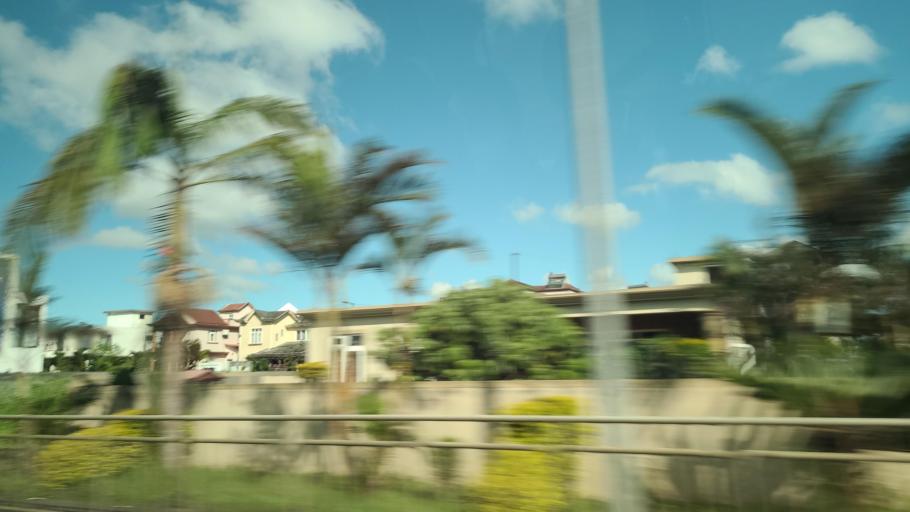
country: MU
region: Moka
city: Providence
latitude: -20.2465
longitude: 57.6093
